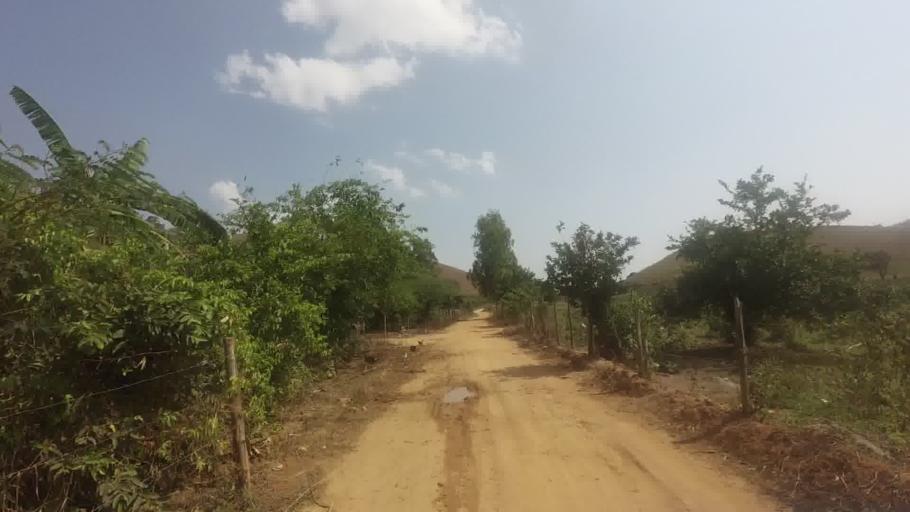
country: BR
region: Espirito Santo
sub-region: Sao Jose Do Calcado
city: Sao Jose do Calcado
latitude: -21.0334
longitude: -41.5199
